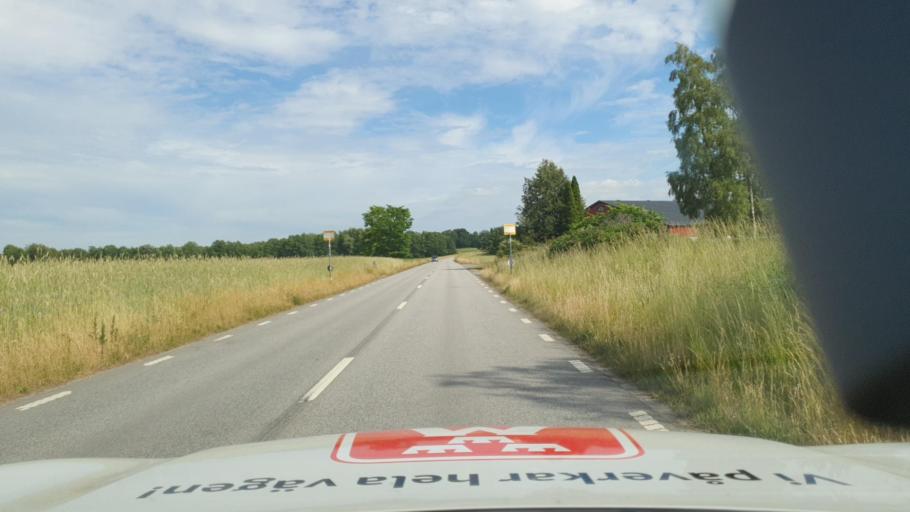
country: SE
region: Skane
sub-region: Sjobo Kommun
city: Blentarp
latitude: 55.6017
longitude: 13.5905
